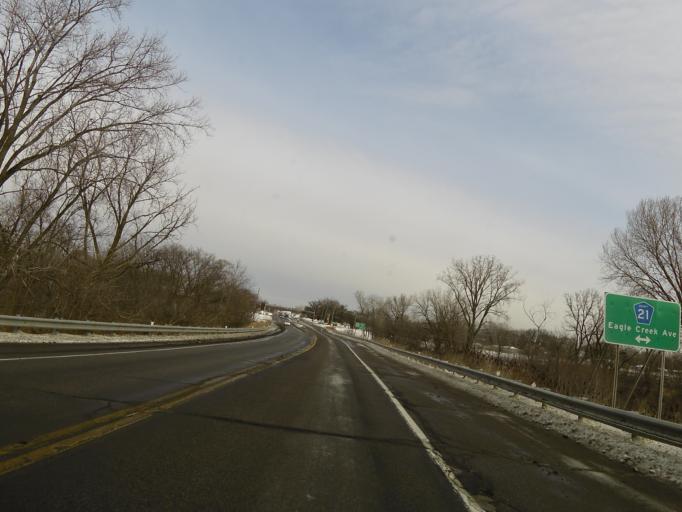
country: US
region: Minnesota
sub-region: Scott County
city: Prior Lake
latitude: 44.7108
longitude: -93.4240
